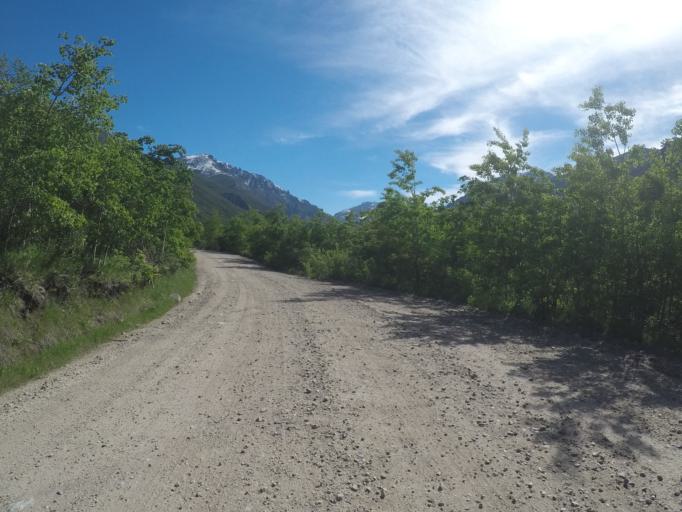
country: US
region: Montana
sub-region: Stillwater County
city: Absarokee
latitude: 45.2582
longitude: -109.5665
